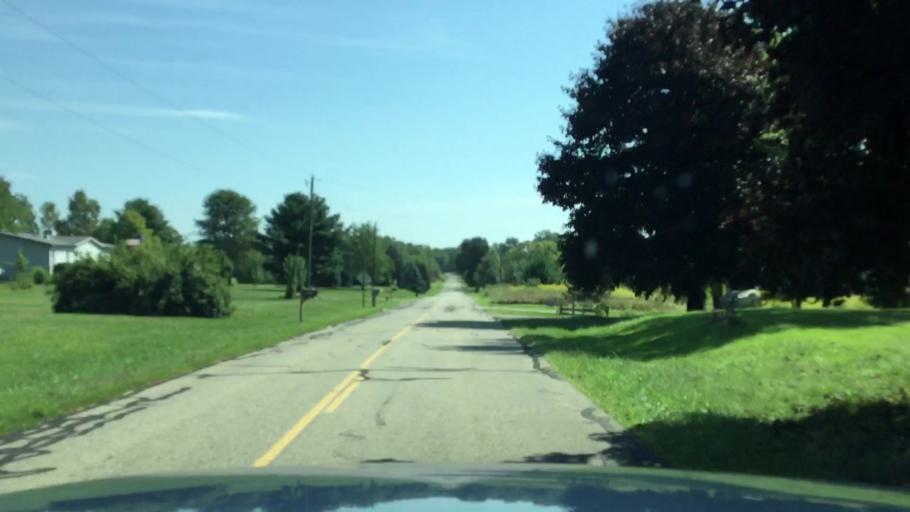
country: US
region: Michigan
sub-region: Lenawee County
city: Manitou Beach-Devils Lake
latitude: 42.0083
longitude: -84.3144
